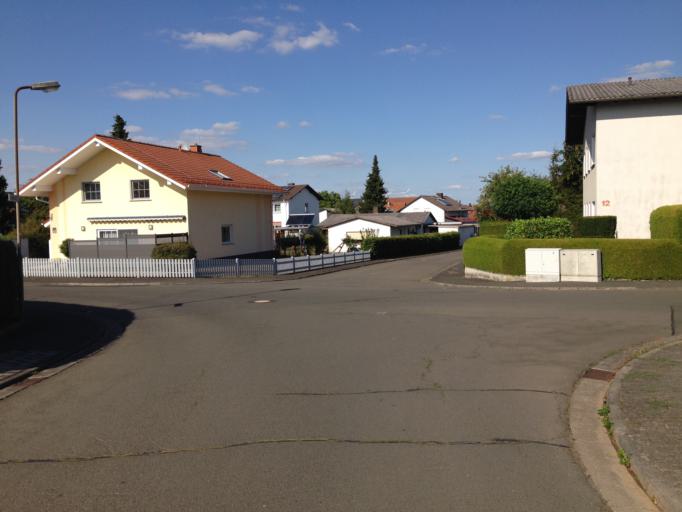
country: DE
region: Hesse
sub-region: Regierungsbezirk Giessen
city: Grunberg
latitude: 50.6191
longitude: 8.9029
